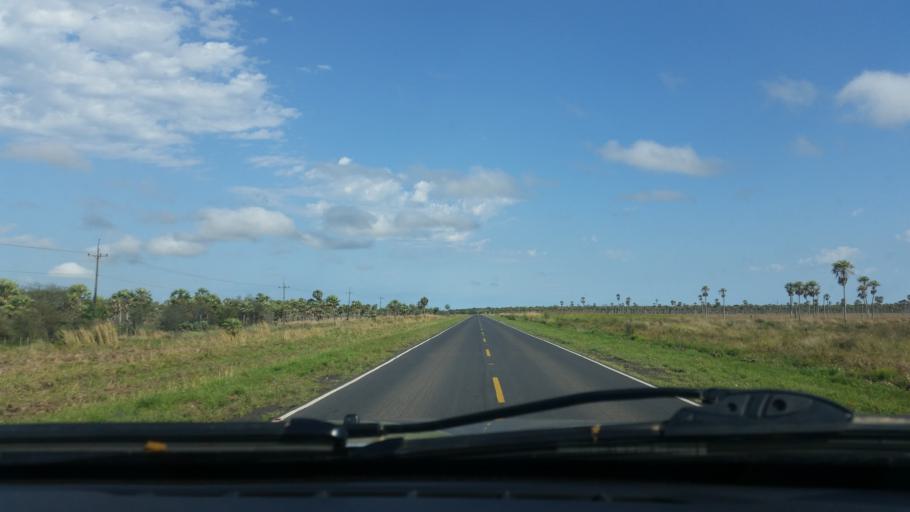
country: PY
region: Presidente Hayes
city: Benjamin Aceval
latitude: -24.9133
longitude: -57.6222
